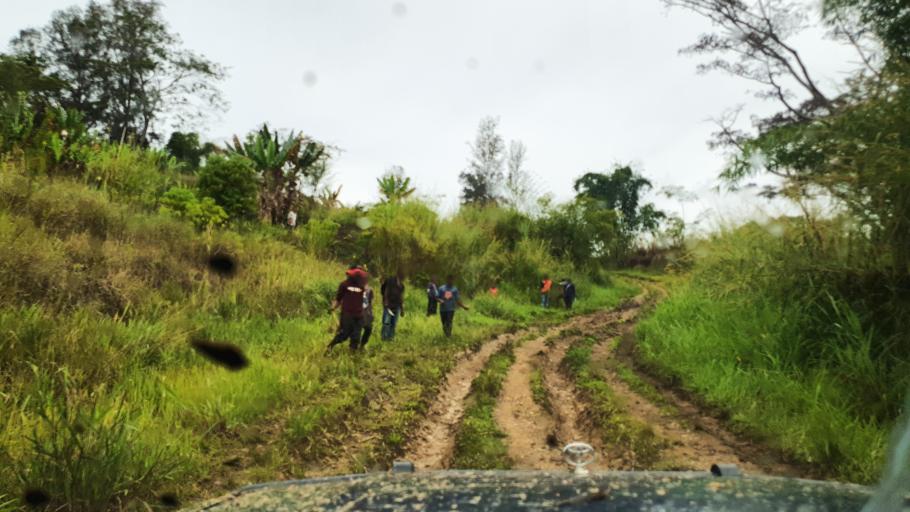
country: PG
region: Jiwaka
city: Minj
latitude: -5.9551
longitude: 144.7786
